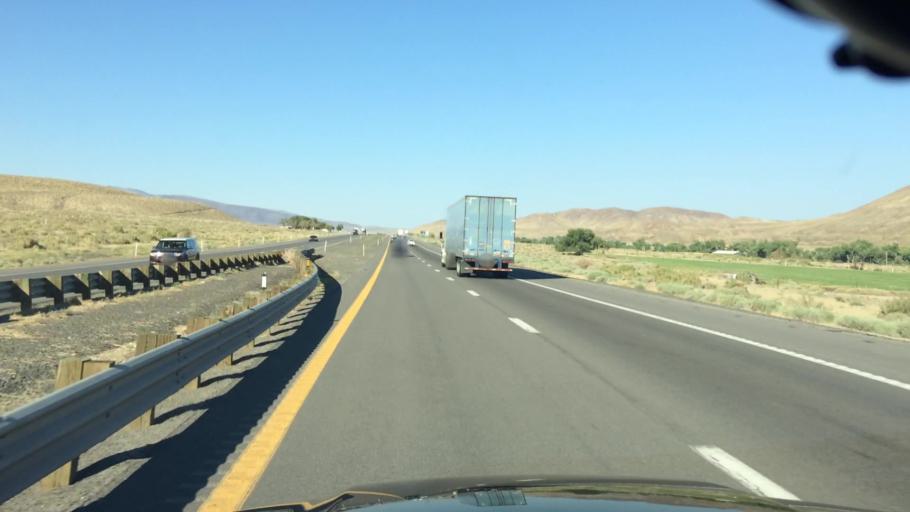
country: US
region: Nevada
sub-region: Lyon County
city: Fernley
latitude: 39.5992
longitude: -119.3461
